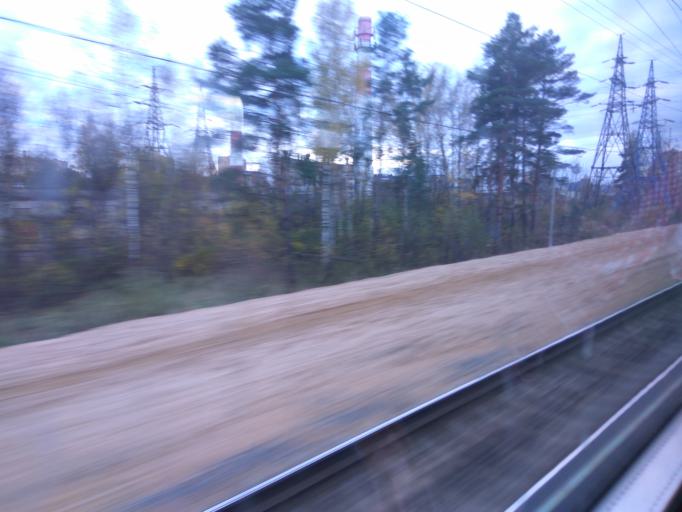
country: RU
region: Moskovskaya
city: Selyatino
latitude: 55.5218
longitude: 36.9783
